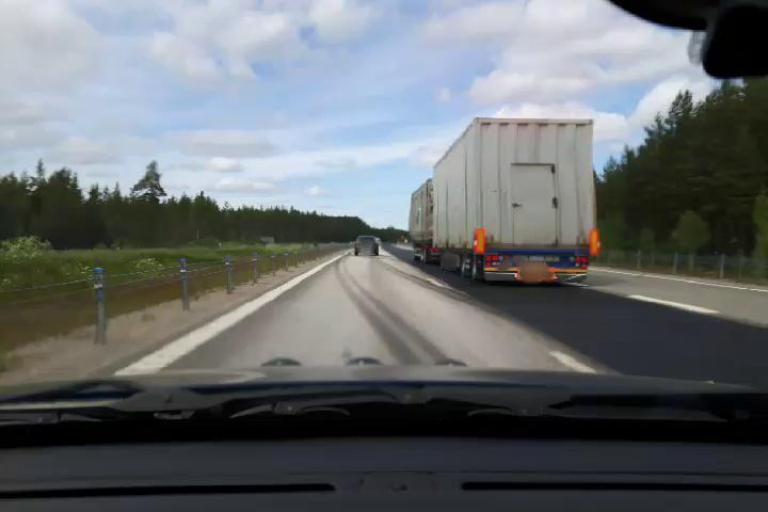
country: SE
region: Uppsala
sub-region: Alvkarleby Kommun
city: AElvkarleby
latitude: 60.4430
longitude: 17.4188
